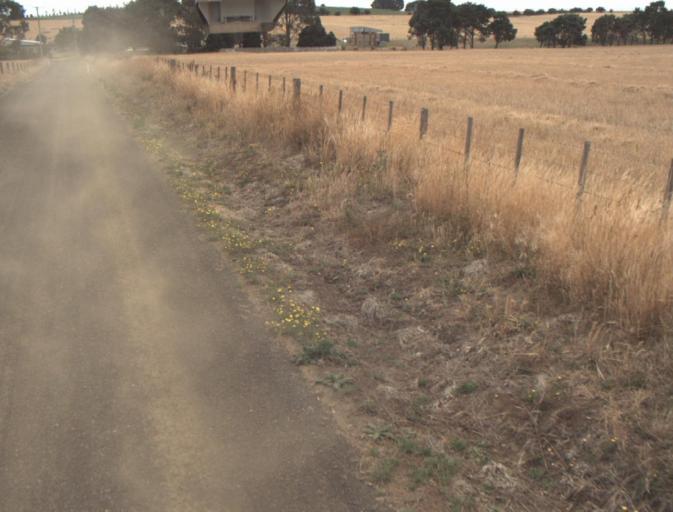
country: AU
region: Tasmania
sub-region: Northern Midlands
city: Evandale
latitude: -41.5273
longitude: 147.2720
